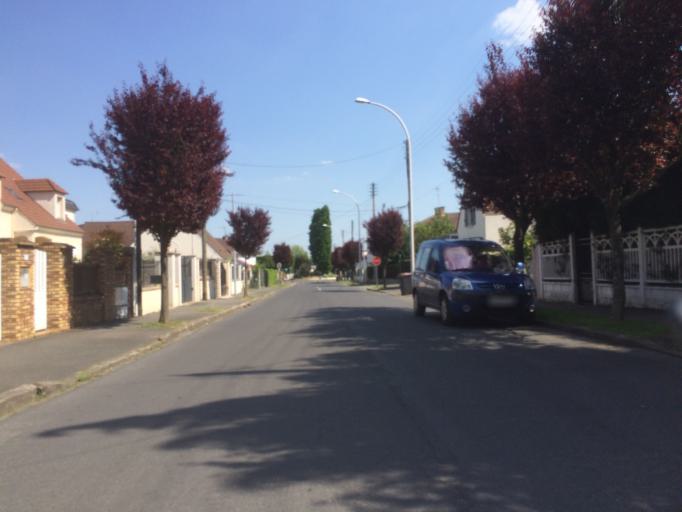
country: FR
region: Ile-de-France
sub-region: Departement de l'Essonne
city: Savigny-sur-Orge
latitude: 48.6914
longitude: 2.3496
